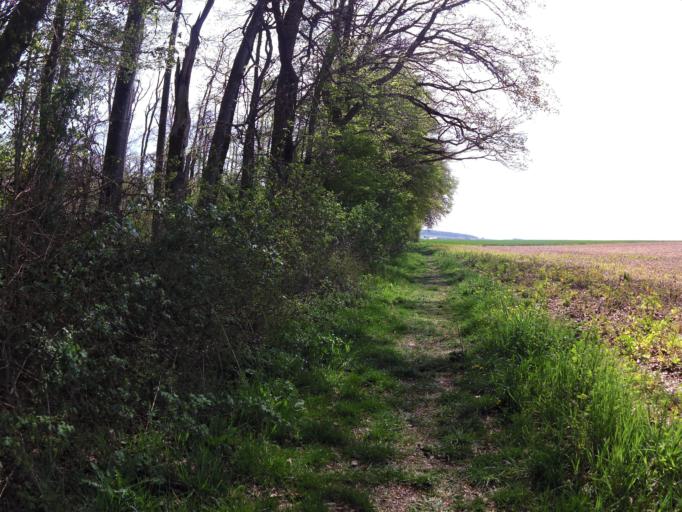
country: DE
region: Bavaria
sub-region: Regierungsbezirk Unterfranken
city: Rimpar
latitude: 49.8614
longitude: 9.9789
